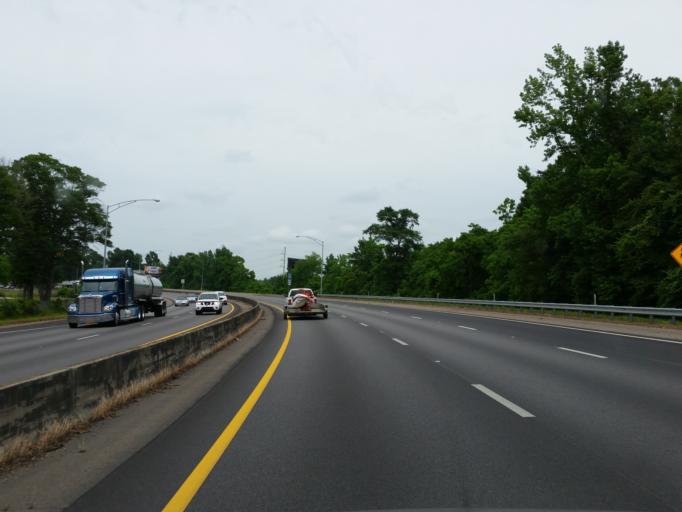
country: US
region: Mississippi
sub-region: Jones County
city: Laurel
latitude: 31.6897
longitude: -89.1188
